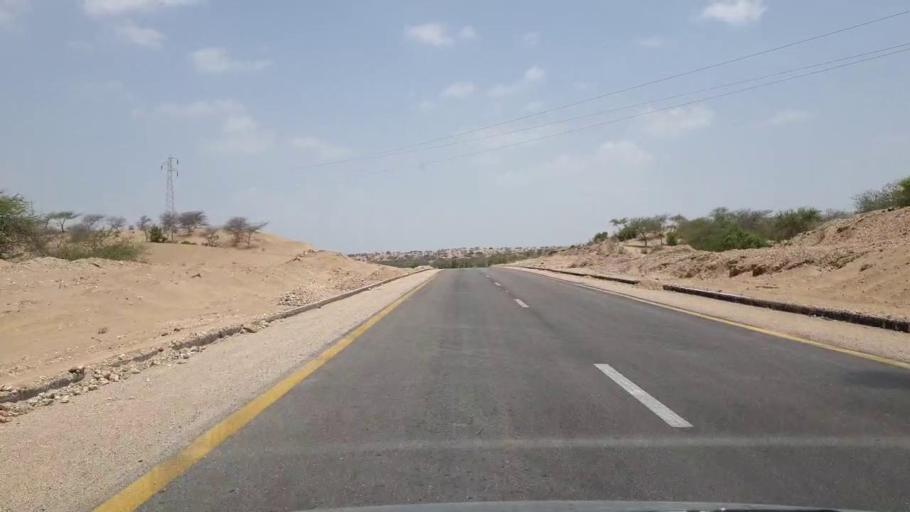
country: PK
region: Sindh
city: Mithi
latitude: 24.8173
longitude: 69.7033
